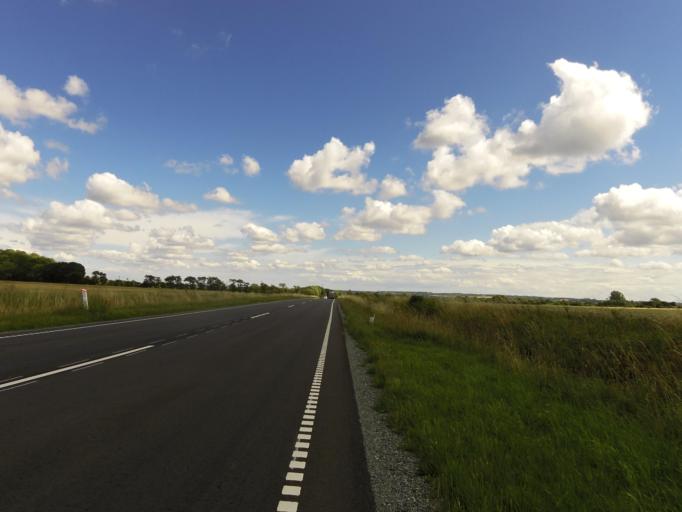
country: DK
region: South Denmark
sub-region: Haderslev Kommune
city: Gram
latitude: 55.3113
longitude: 9.1253
